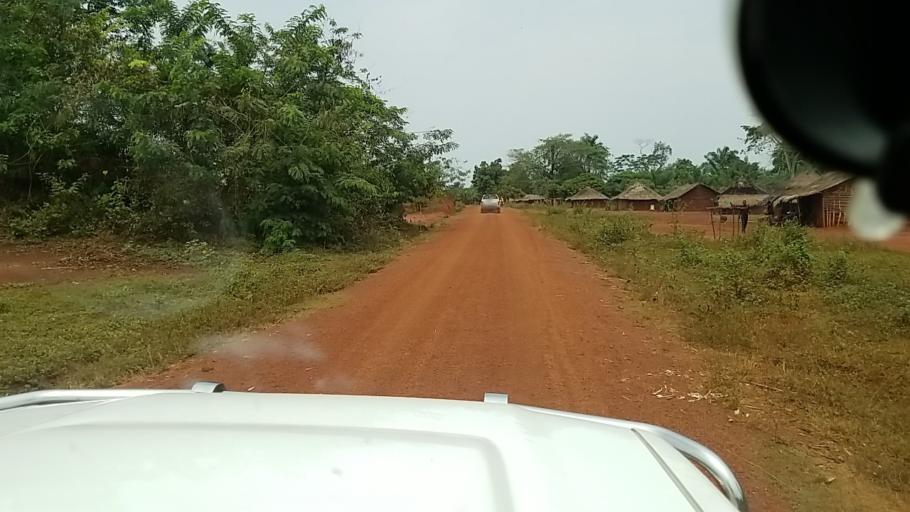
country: CD
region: Equateur
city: Gemena
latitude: 3.5217
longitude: 19.3653
